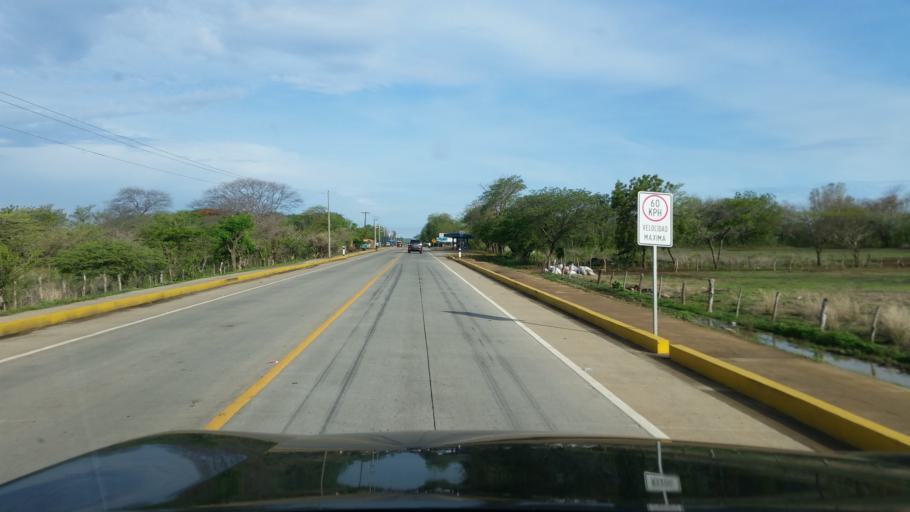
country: NI
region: Managua
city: Carlos Fonseca Amador
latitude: 12.1019
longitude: -86.5748
